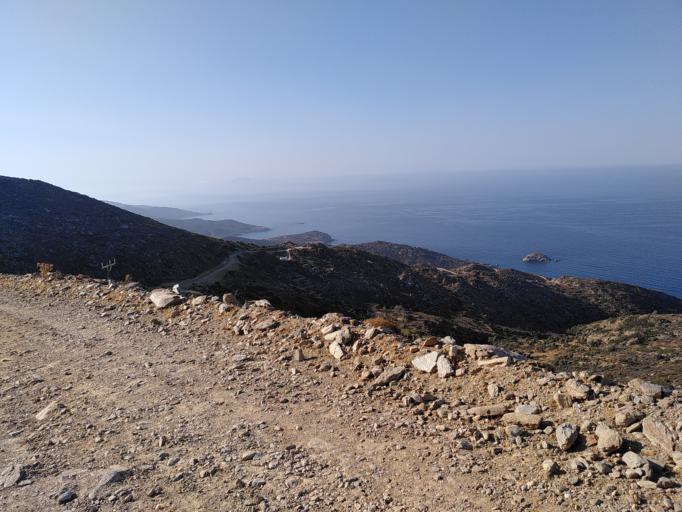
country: GR
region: South Aegean
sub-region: Nomos Kykladon
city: Ios
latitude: 36.7021
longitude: 25.3147
